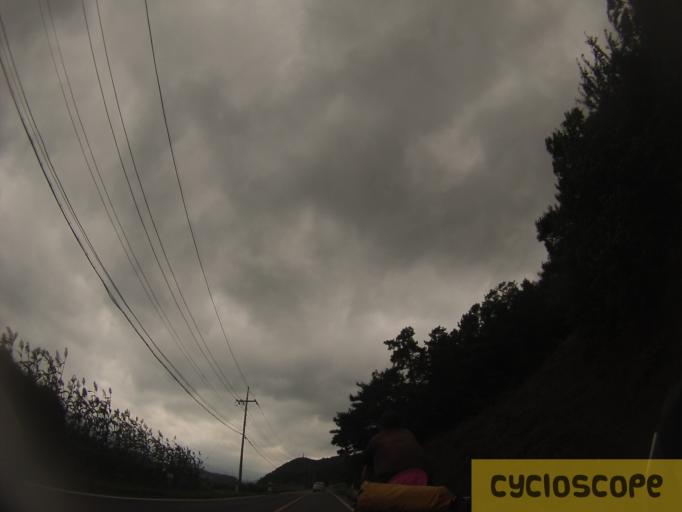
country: KR
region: Chungcheongnam-do
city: Yesan
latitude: 36.5777
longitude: 126.7912
